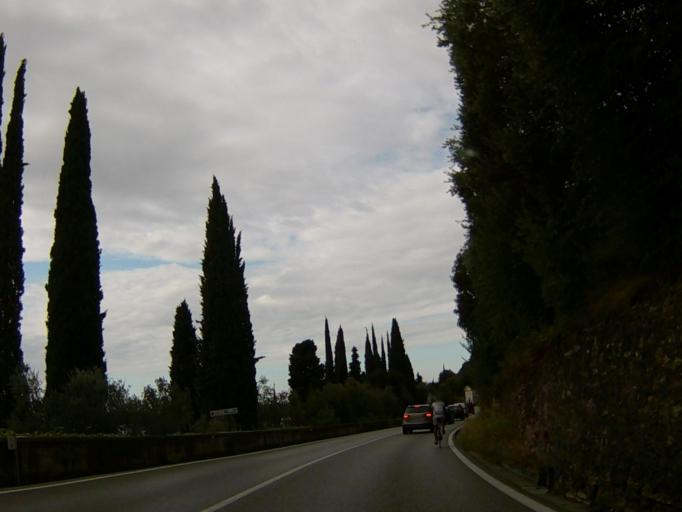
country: IT
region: Lombardy
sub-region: Provincia di Brescia
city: Toscolano Maderno
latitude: 45.6508
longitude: 10.6281
